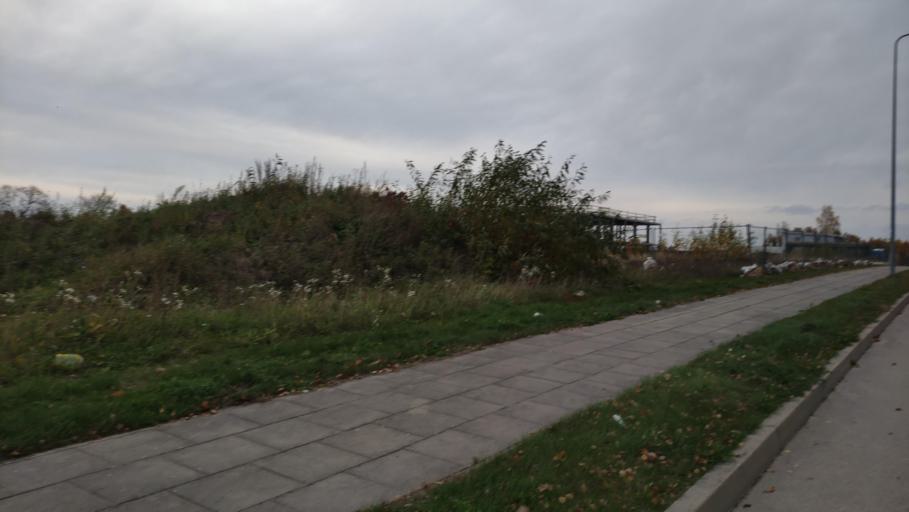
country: LT
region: Alytaus apskritis
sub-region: Alytus
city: Alytus
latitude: 54.4275
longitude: 24.0258
